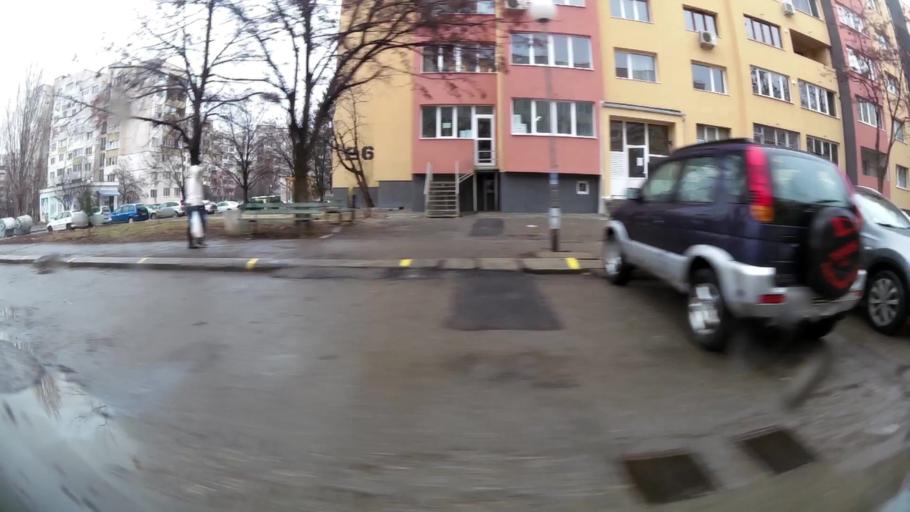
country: BG
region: Sofia-Capital
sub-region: Stolichna Obshtina
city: Sofia
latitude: 42.6499
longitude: 23.4022
